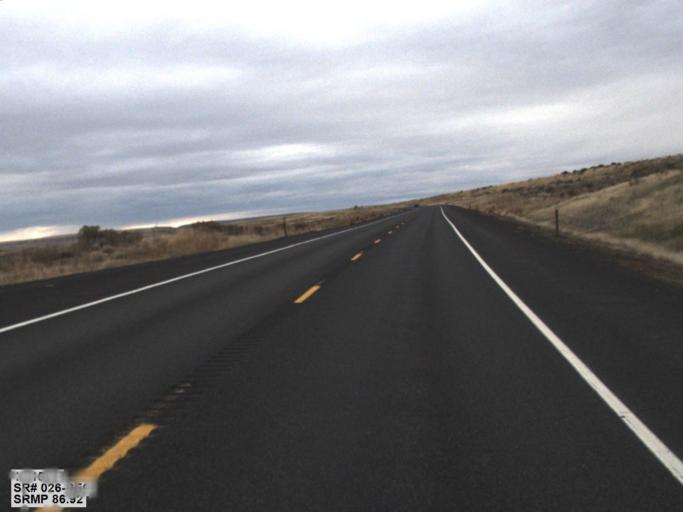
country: US
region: Washington
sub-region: Adams County
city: Ritzville
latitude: 46.7426
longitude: -118.2314
